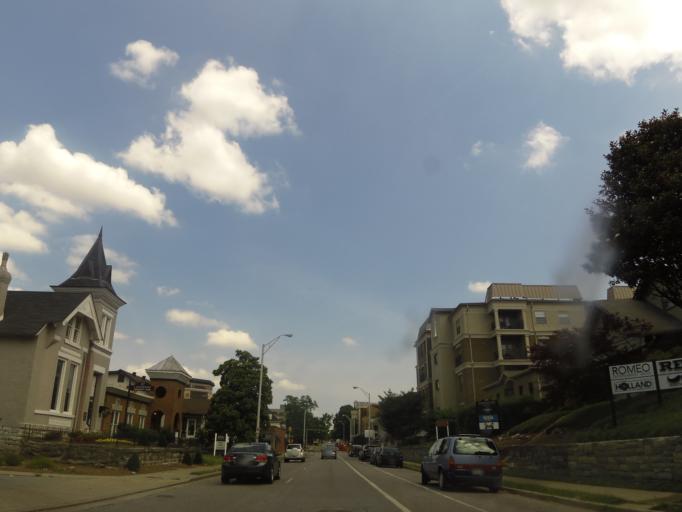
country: US
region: Tennessee
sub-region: Davidson County
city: Nashville
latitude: 36.1456
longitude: -86.7927
